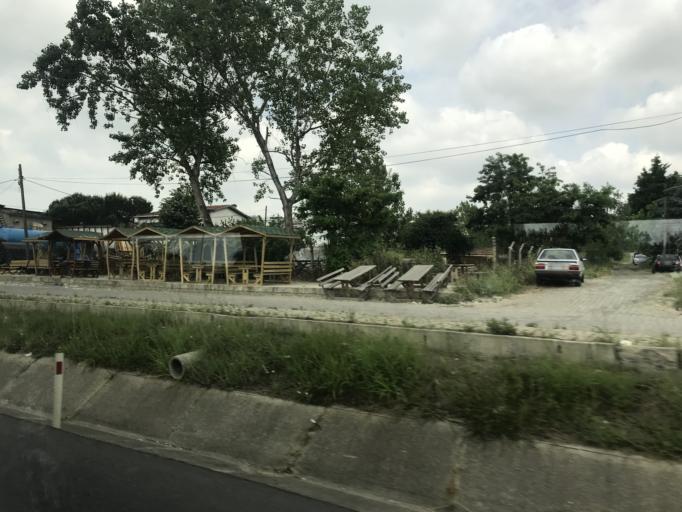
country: TR
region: Tekirdag
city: Corlu
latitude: 41.0083
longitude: 27.7115
